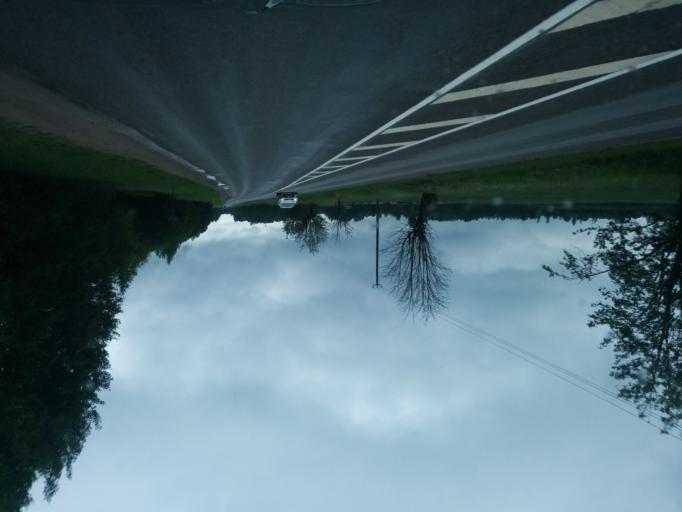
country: LV
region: Smiltene
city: Smiltene
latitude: 57.3916
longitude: 25.9710
